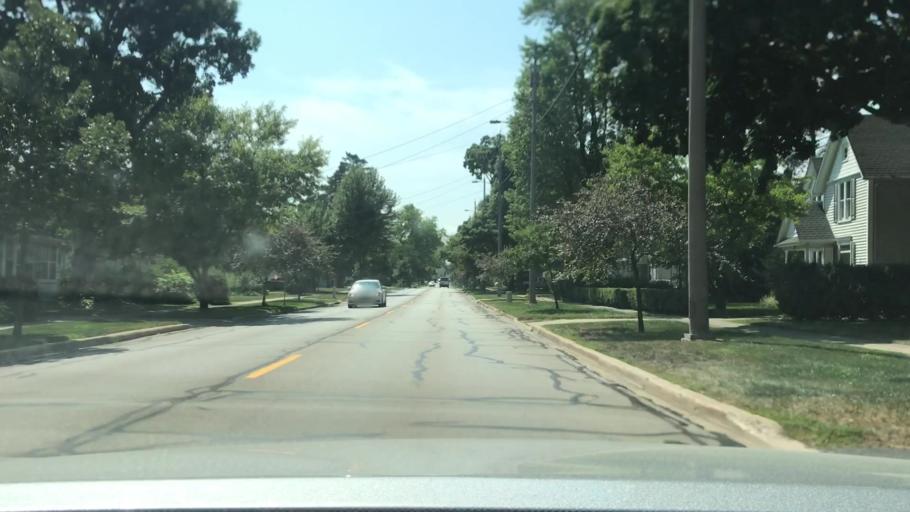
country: US
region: Illinois
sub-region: Kane County
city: Batavia
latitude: 41.8511
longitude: -88.2951
